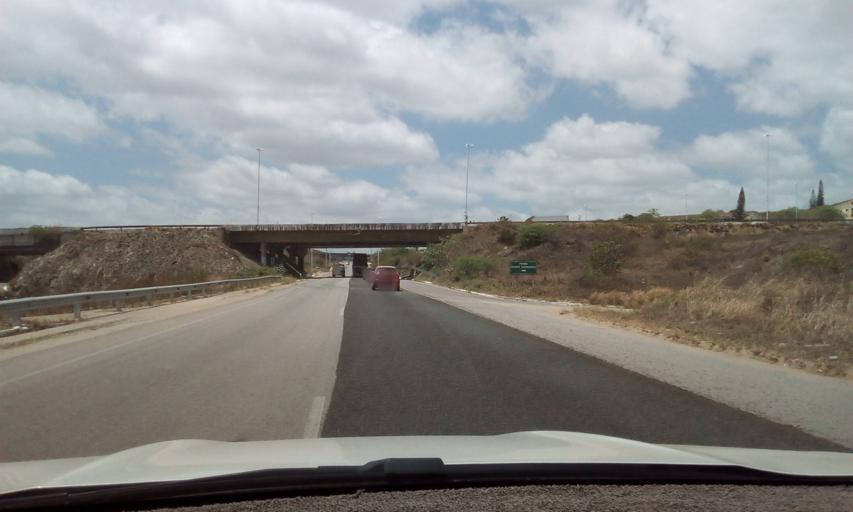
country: BR
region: Pernambuco
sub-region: Caruaru
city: Caruaru
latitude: -8.2990
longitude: -35.9886
